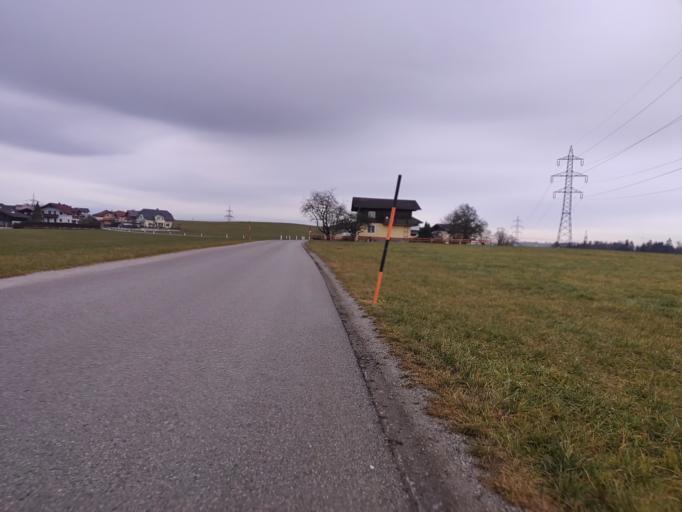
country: AT
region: Salzburg
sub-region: Politischer Bezirk Salzburg-Umgebung
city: Elixhausen
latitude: 47.8914
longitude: 13.0573
